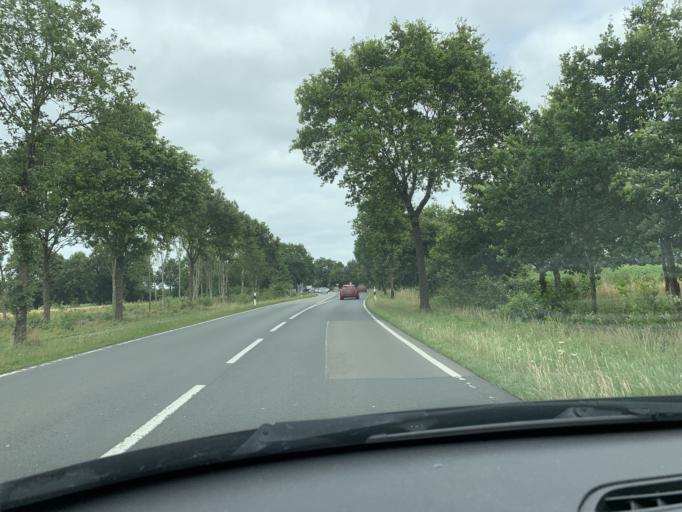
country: DE
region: Lower Saxony
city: Westerstede
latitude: 53.2737
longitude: 7.9565
